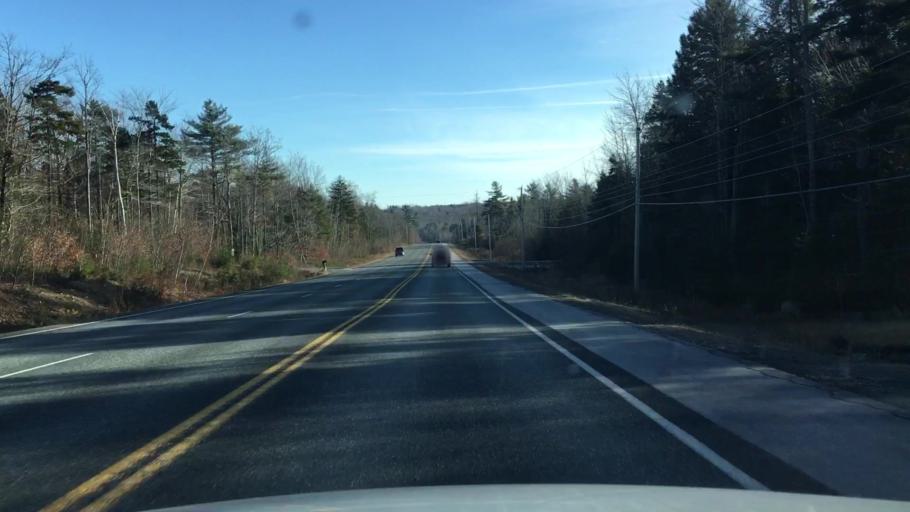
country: US
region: Maine
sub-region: Hancock County
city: Dedham
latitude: 44.6403
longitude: -68.5515
